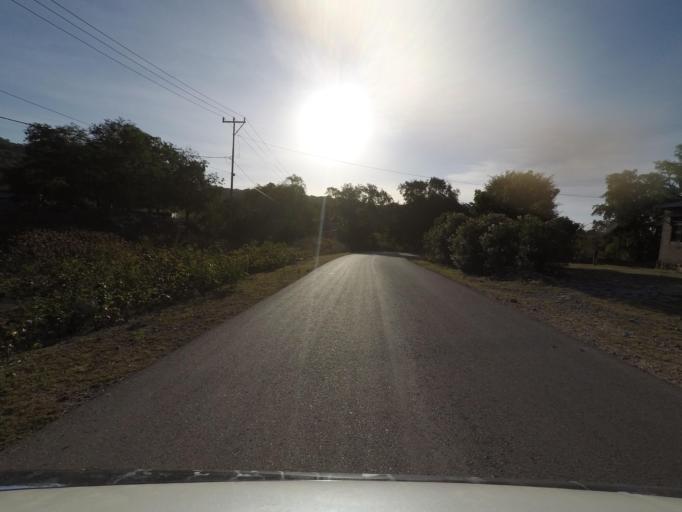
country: TL
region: Lautem
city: Lospalos
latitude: -8.3579
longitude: 127.0563
